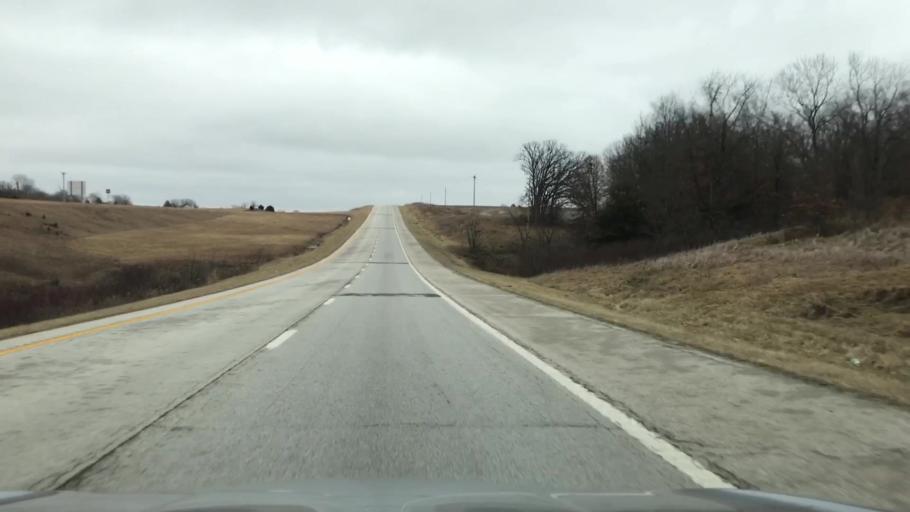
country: US
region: Missouri
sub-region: Linn County
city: Marceline
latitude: 39.7602
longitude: -92.9242
